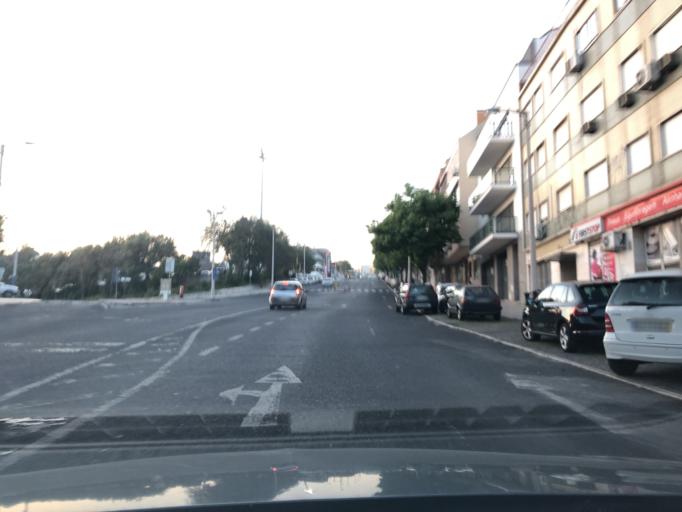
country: PT
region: Lisbon
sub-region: Oeiras
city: Alges
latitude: 38.7001
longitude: -9.2059
